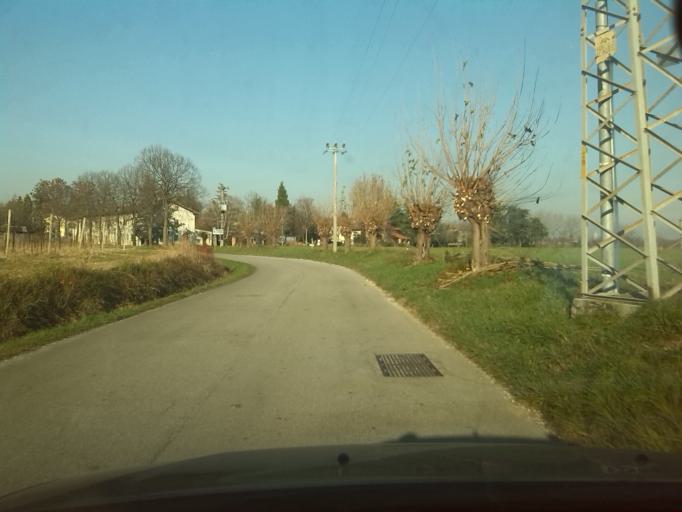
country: IT
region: Friuli Venezia Giulia
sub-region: Provincia di Udine
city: Santa Maria la Longa
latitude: 45.9203
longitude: 13.2788
